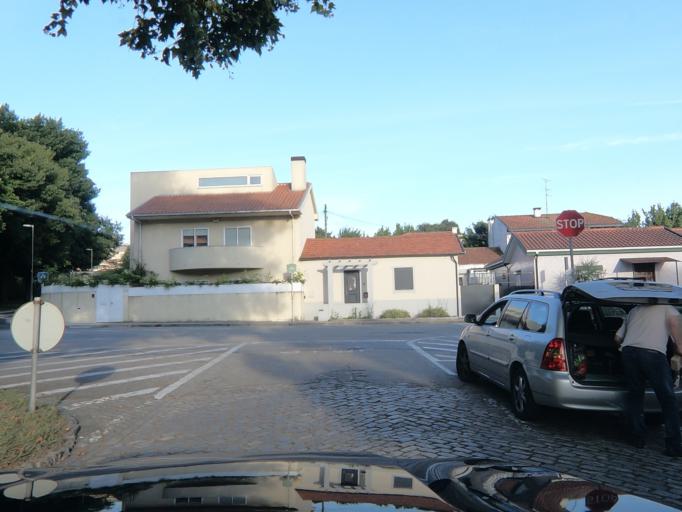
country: PT
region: Porto
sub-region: Matosinhos
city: Sao Mamede de Infesta
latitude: 41.1786
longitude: -8.6189
